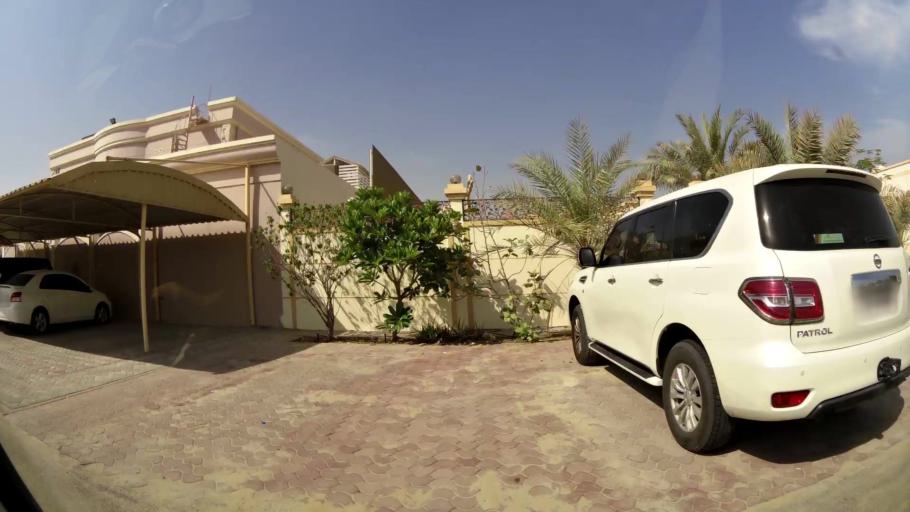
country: AE
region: Ash Shariqah
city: Sharjah
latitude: 25.2686
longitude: 55.4020
